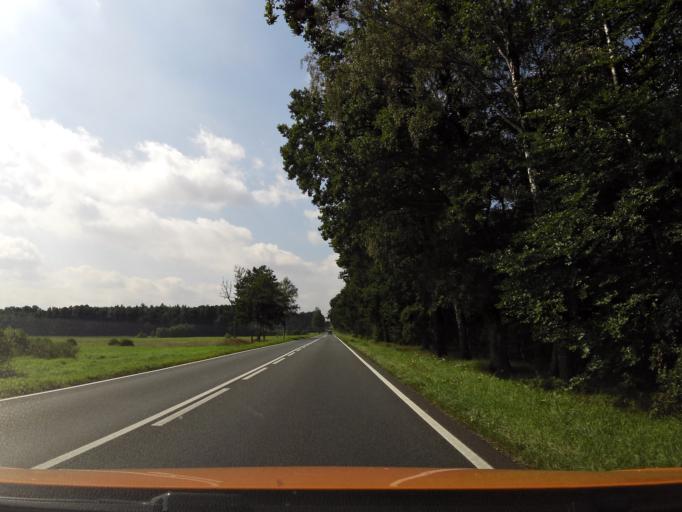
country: PL
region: West Pomeranian Voivodeship
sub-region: Powiat gryficki
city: Ploty
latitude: 53.7622
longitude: 15.2331
